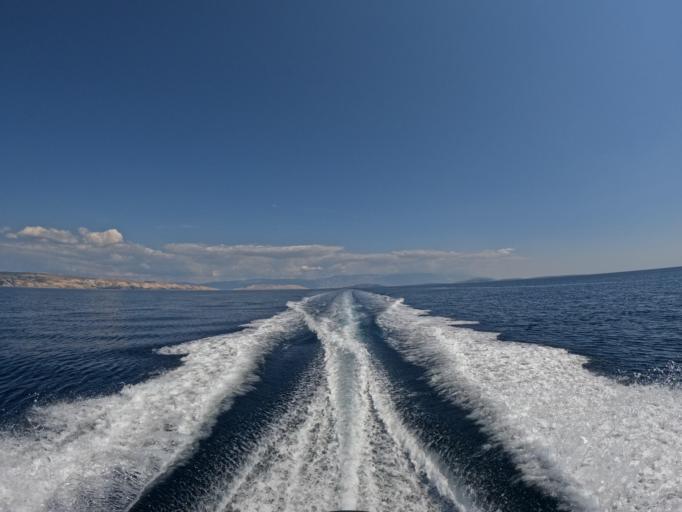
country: HR
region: Primorsko-Goranska
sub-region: Grad Krk
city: Krk
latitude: 44.9226
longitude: 14.5550
